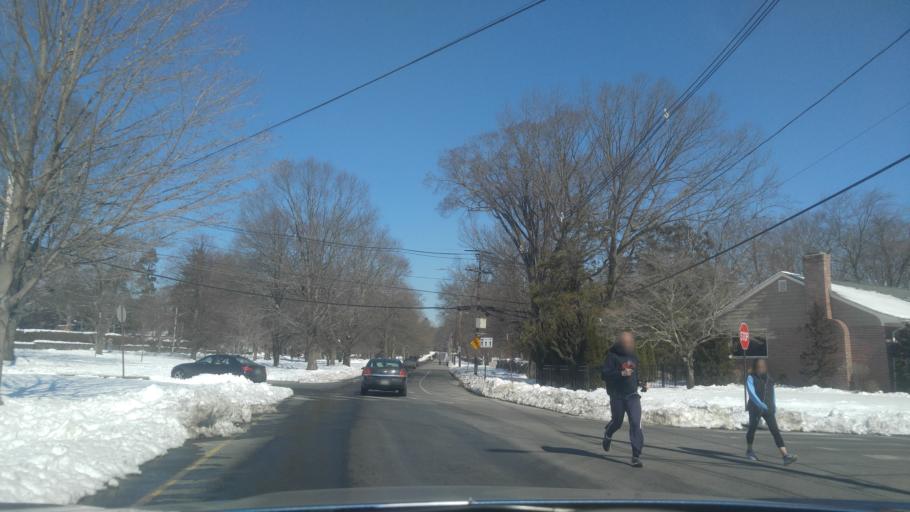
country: US
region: Rhode Island
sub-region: Providence County
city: Providence
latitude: 41.8452
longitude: -71.3867
